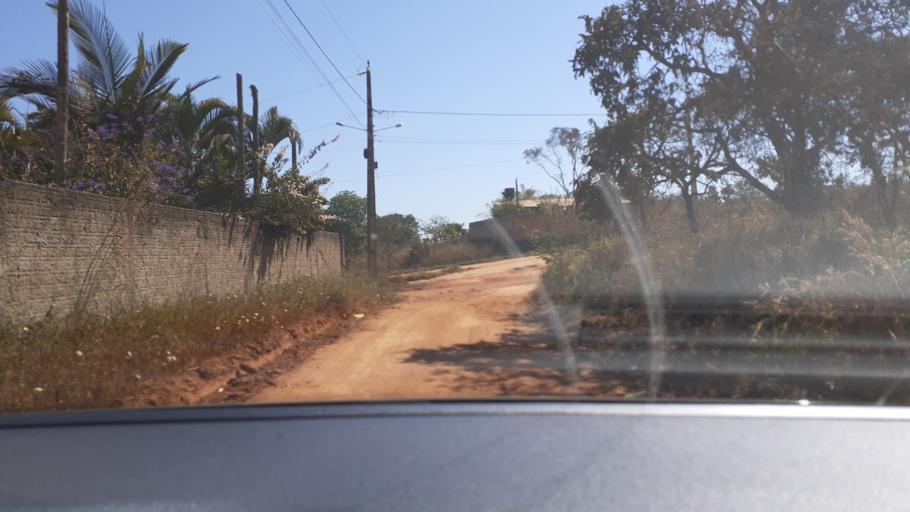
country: BR
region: Goias
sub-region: Aparecida De Goiania
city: Aparecida de Goiania
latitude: -16.8901
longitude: -49.2623
